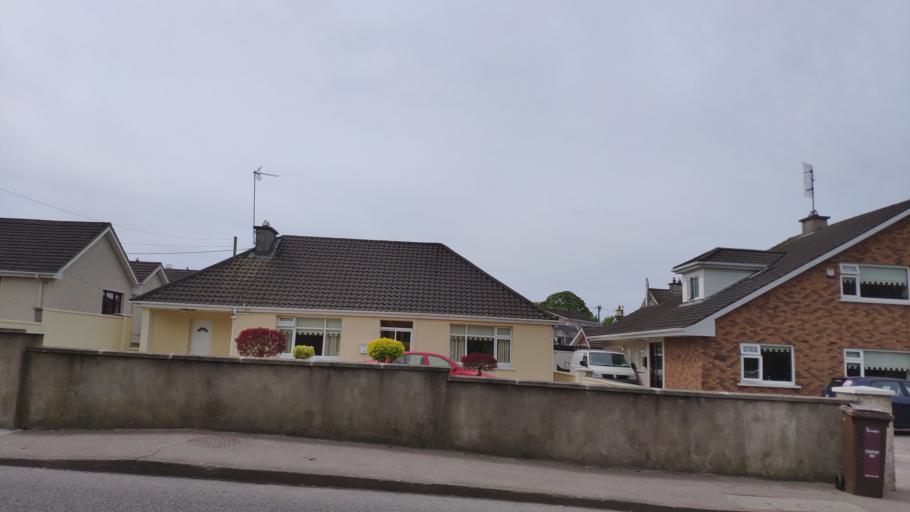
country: IE
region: Munster
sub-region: County Cork
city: Cork
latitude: 51.9194
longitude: -8.4522
